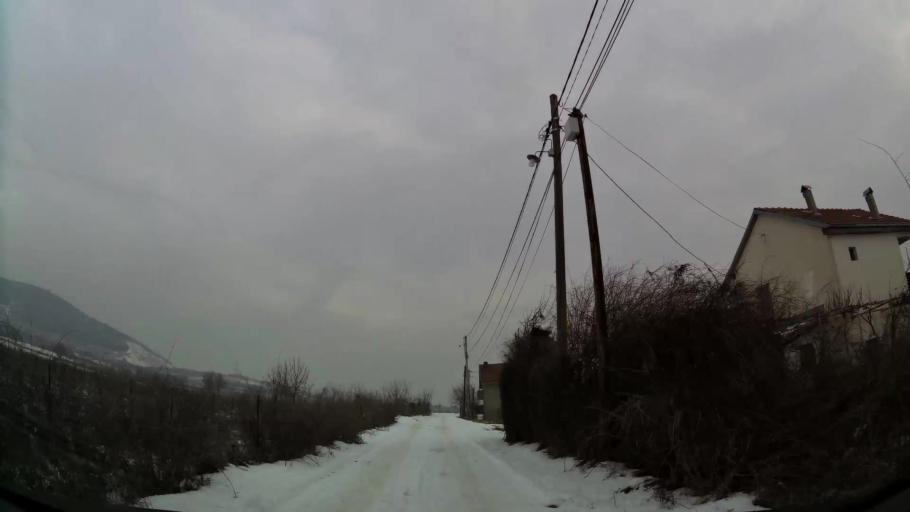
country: MK
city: Kondovo
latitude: 42.0393
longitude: 21.3398
